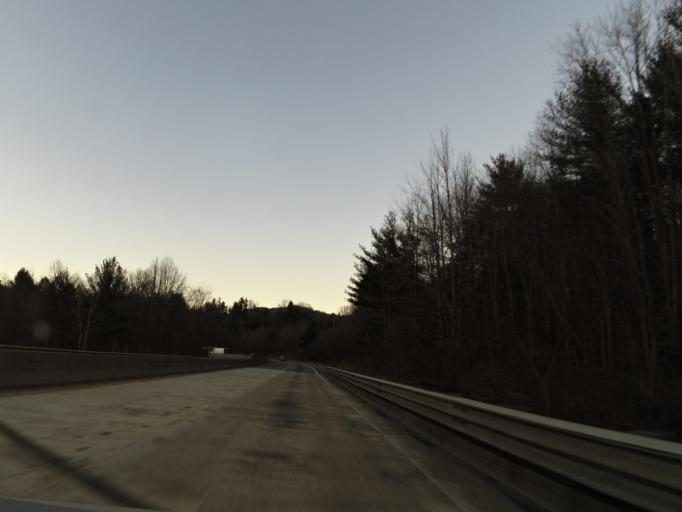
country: US
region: North Carolina
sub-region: Haywood County
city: Cove Creek
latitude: 35.6637
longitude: -82.9901
